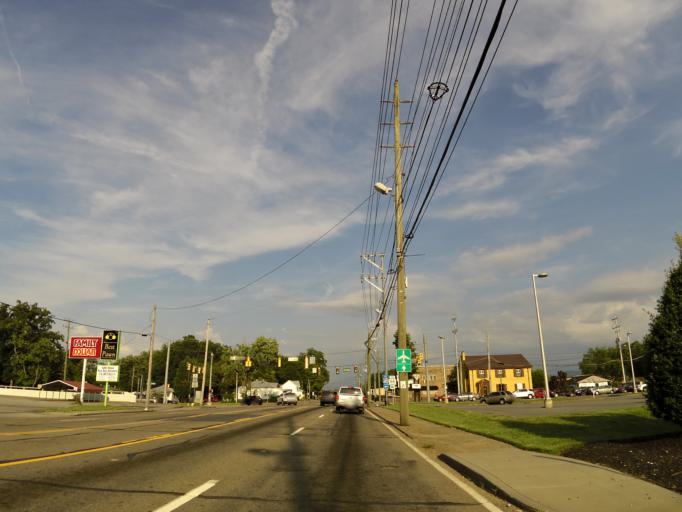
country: US
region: Tennessee
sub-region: Sevier County
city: Sevierville
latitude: 35.8686
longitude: -83.5639
